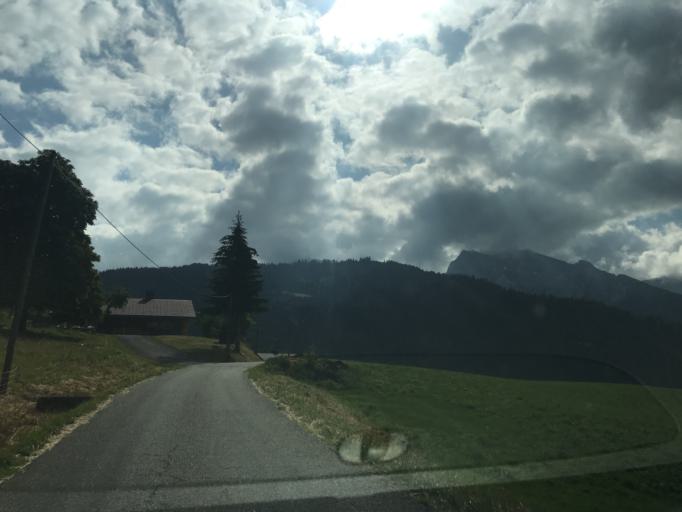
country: FR
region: Rhone-Alpes
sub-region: Departement de la Haute-Savoie
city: La Clusaz
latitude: 45.8683
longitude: 6.3811
